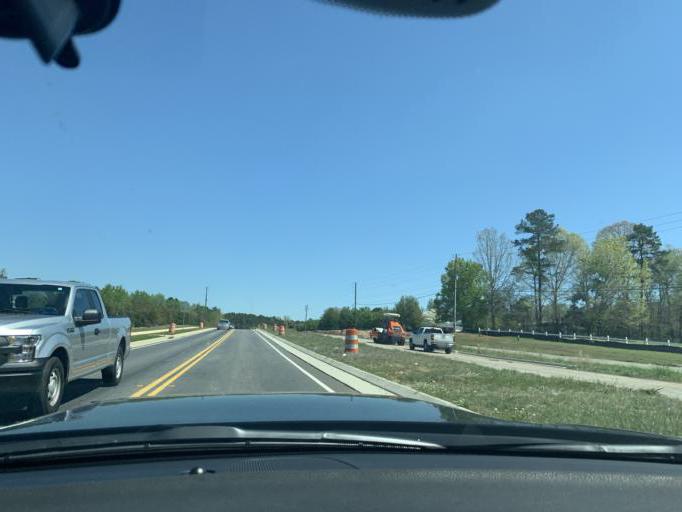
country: US
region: Georgia
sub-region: Forsyth County
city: Cumming
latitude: 34.2228
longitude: -84.1958
